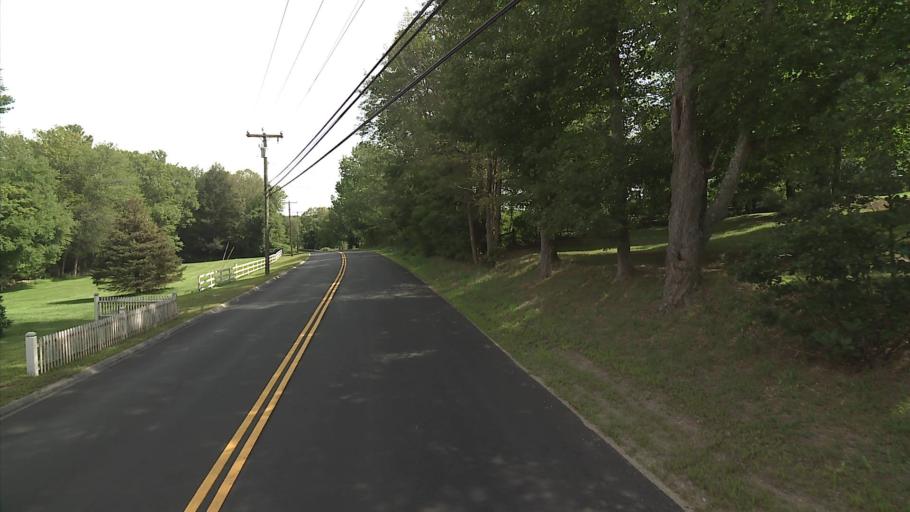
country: US
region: Connecticut
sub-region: Windham County
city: South Woodstock
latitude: 41.9341
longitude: -72.0769
